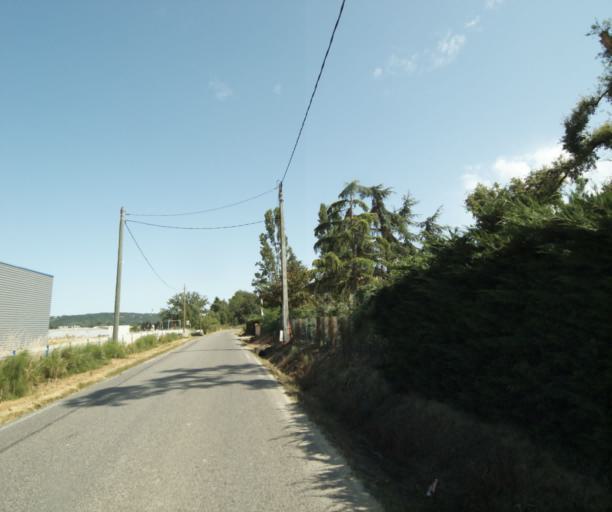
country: FR
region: Midi-Pyrenees
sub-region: Departement du Tarn-et-Garonne
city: Bressols
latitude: 43.9833
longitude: 1.3262
